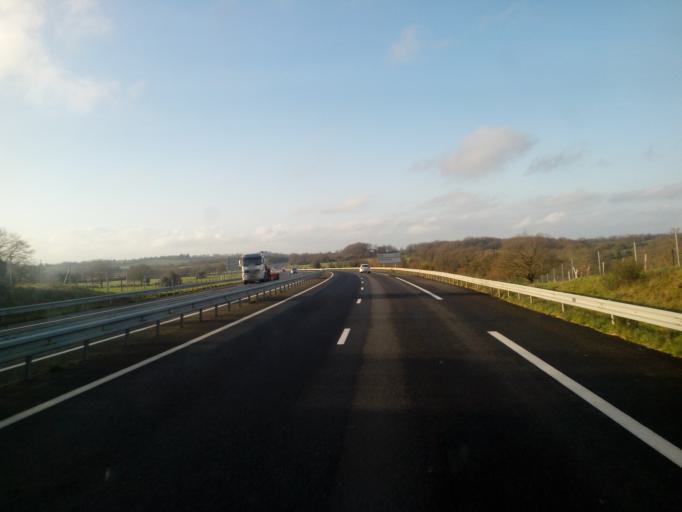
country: FR
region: Pays de la Loire
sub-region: Departement de Maine-et-Loire
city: La Tessoualle
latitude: 46.9818
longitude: -0.8229
